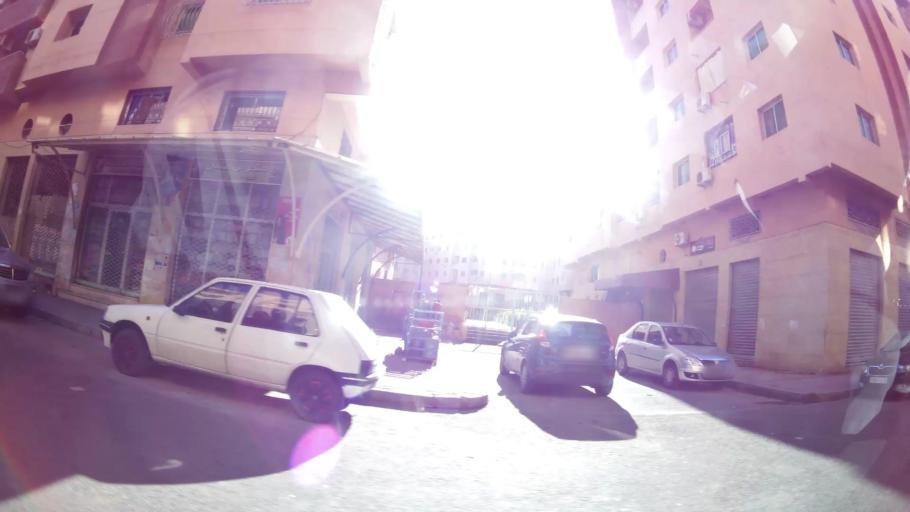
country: MA
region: Marrakech-Tensift-Al Haouz
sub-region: Marrakech
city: Marrakesh
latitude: 31.6516
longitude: -8.0184
